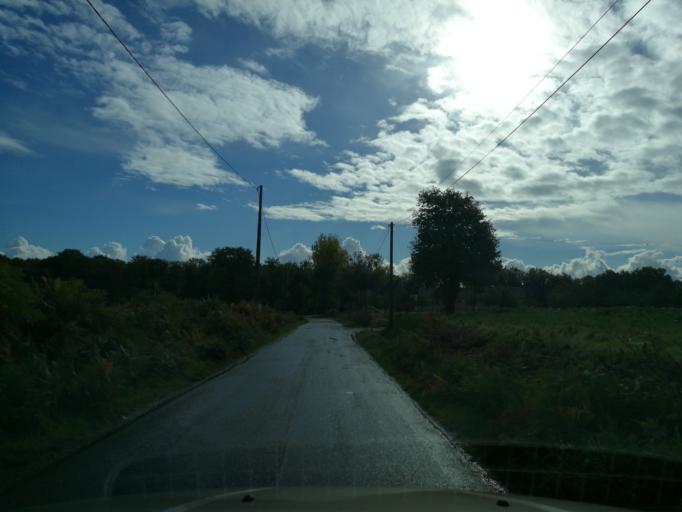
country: FR
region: Brittany
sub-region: Departement d'Ille-et-Vilaine
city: Pleumeleuc
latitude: 48.2055
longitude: -1.9327
